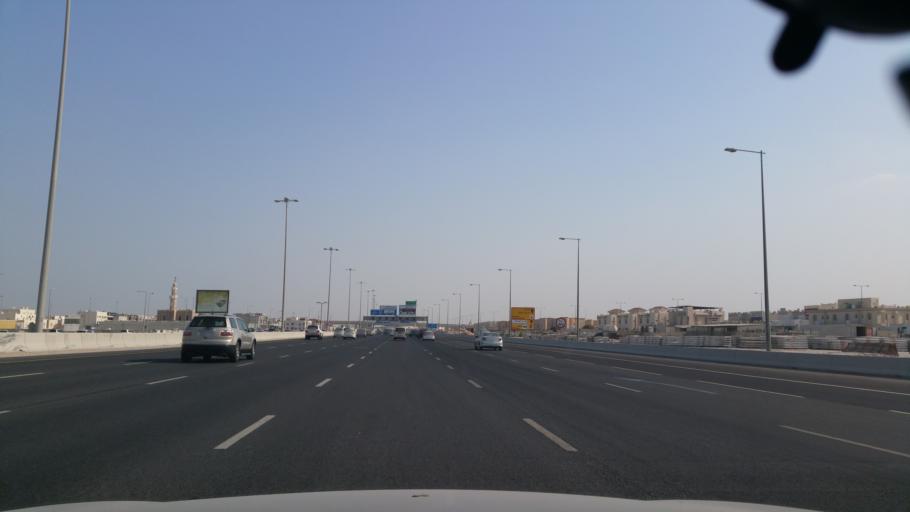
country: QA
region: Baladiyat ar Rayyan
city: Ar Rayyan
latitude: 25.3530
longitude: 51.4534
